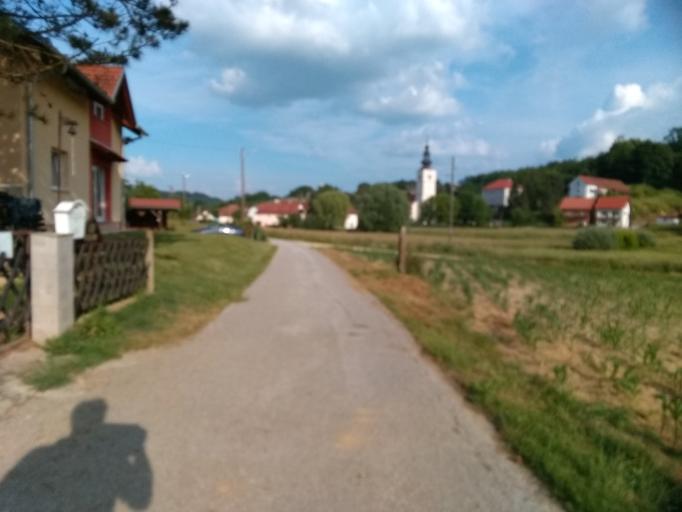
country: SI
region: Bistrica ob Sotli
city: Bistrica ob Sotli
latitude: 46.0761
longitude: 15.7455
